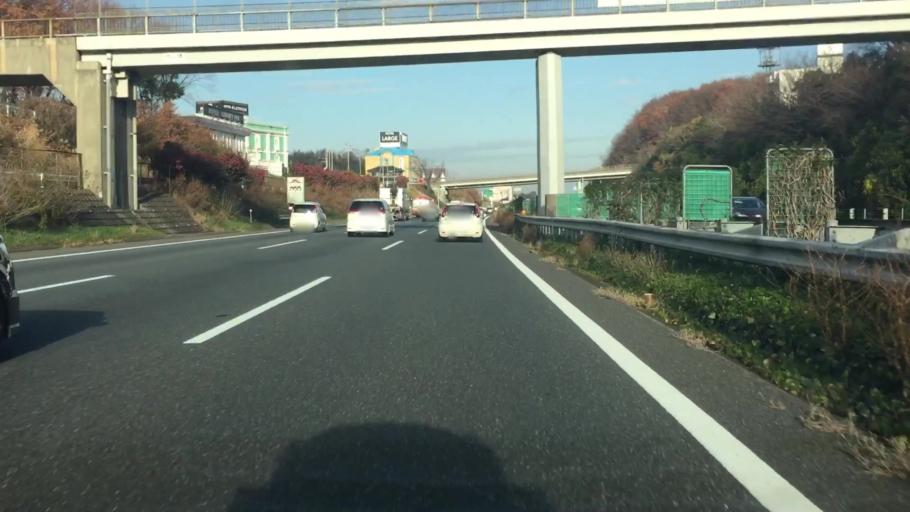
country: JP
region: Saitama
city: Honjo
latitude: 36.2093
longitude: 139.1707
